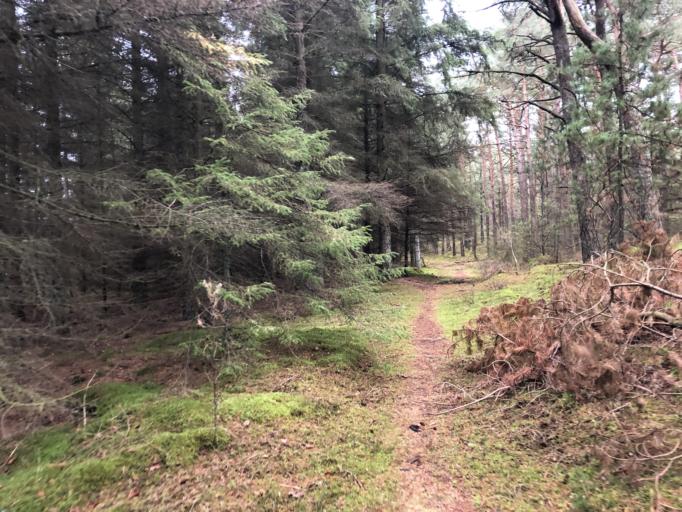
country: DK
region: Central Jutland
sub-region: Holstebro Kommune
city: Ulfborg
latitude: 56.2922
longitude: 8.1676
